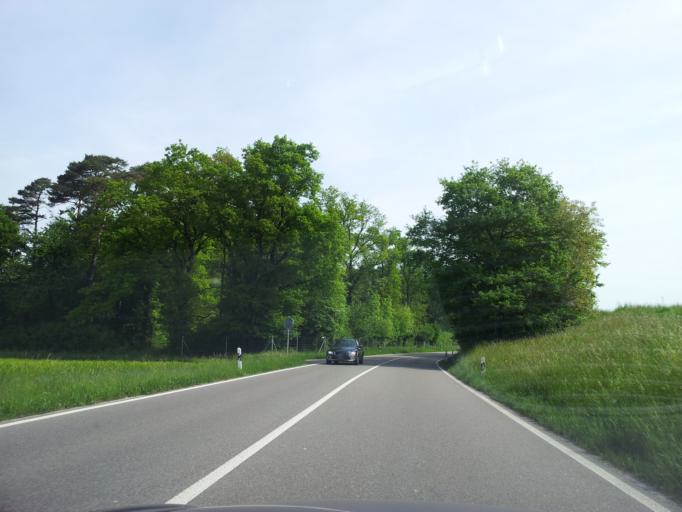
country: CH
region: Zurich
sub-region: Bezirk Buelach
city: Seglingen
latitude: 47.5823
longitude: 8.5182
